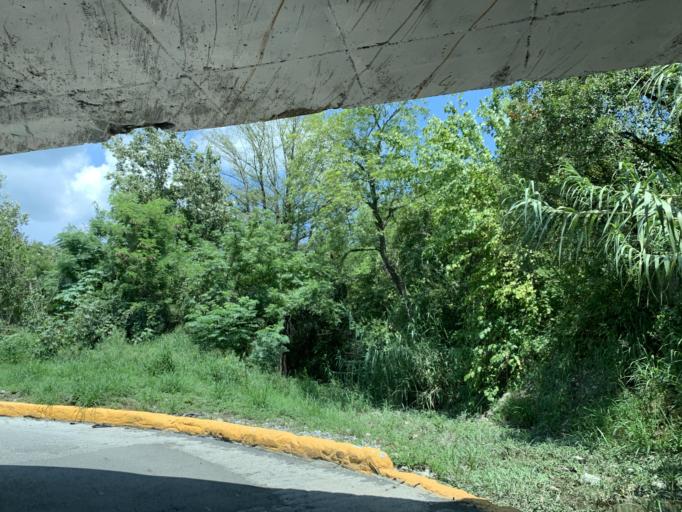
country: MX
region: Nuevo Leon
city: Santiago
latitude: 25.3755
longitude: -100.1097
